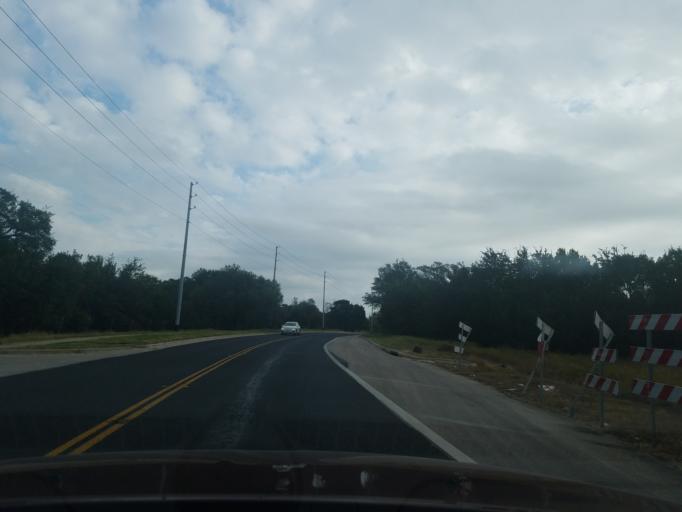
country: US
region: Texas
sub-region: Williamson County
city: Anderson Mill
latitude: 30.4836
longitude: -97.7847
